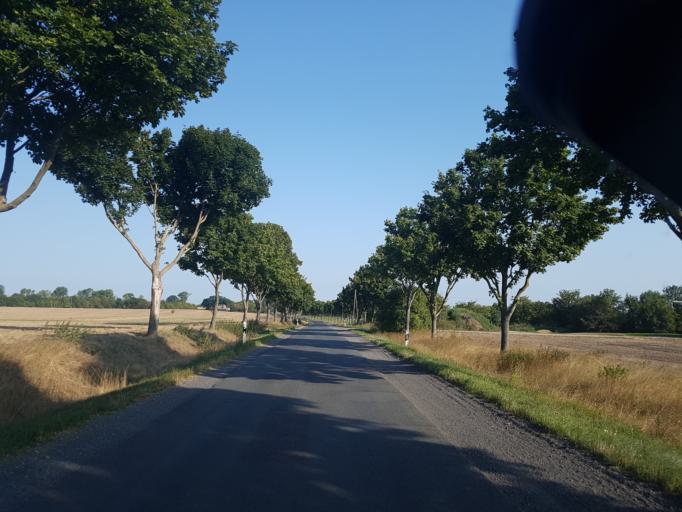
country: DE
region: Brandenburg
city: Niemegk
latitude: 52.0203
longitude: 12.6846
